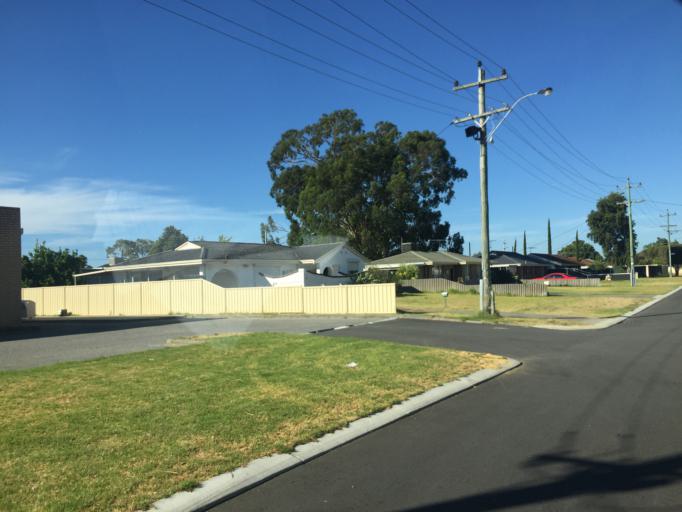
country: AU
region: Western Australia
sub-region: Canning
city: East Cannington
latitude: -32.0142
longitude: 115.9660
